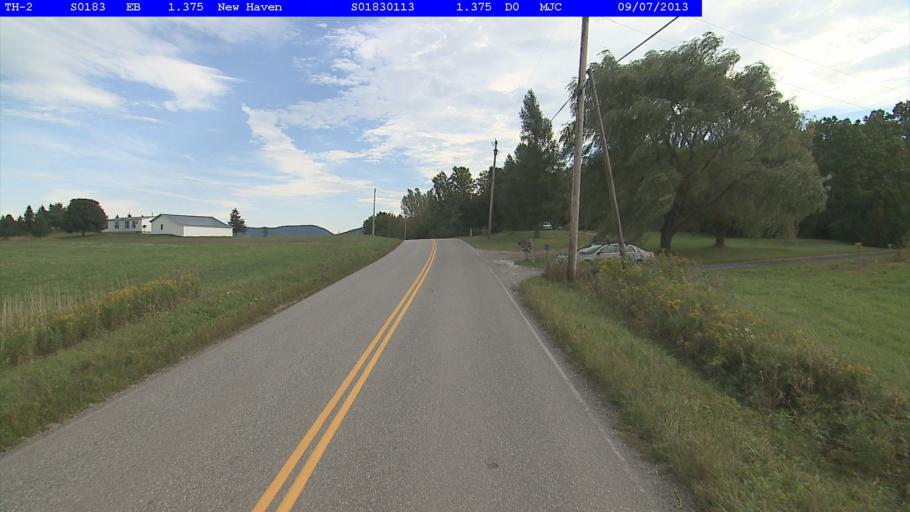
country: US
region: Vermont
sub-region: Addison County
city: Middlebury (village)
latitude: 44.0650
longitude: -73.1463
